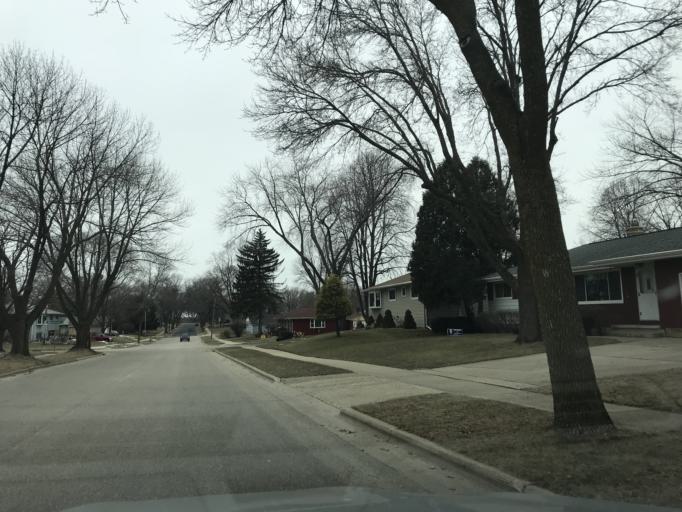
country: US
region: Wisconsin
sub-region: Dane County
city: Monona
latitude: 43.0920
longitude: -89.3001
